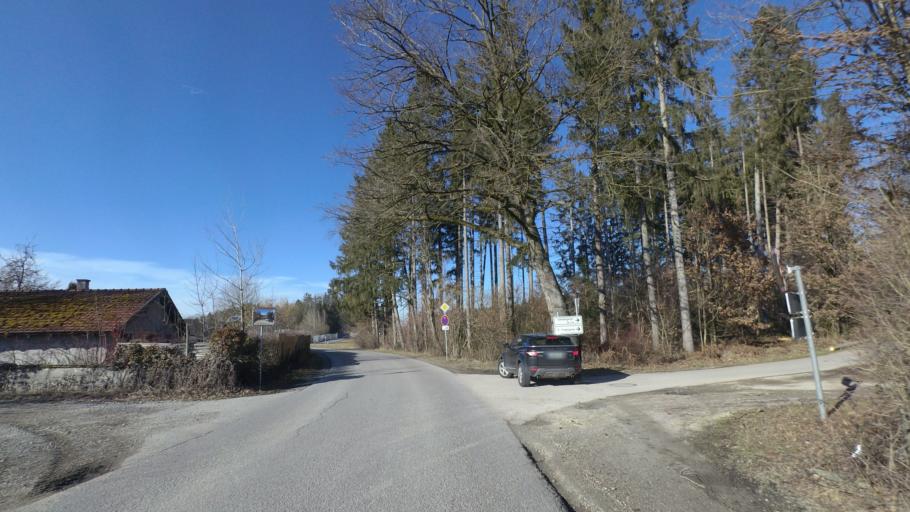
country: DE
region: Bavaria
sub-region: Upper Bavaria
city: Traunreut
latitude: 47.9543
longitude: 12.6183
